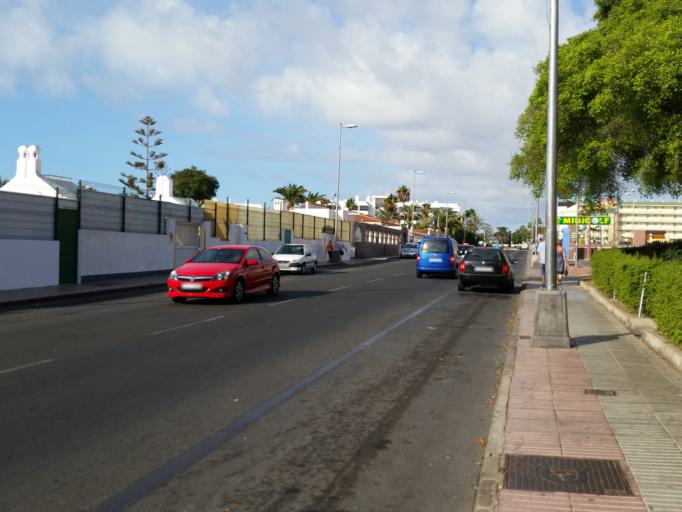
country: ES
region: Canary Islands
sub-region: Provincia de Las Palmas
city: Playa del Ingles
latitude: 27.7576
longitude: -15.5756
